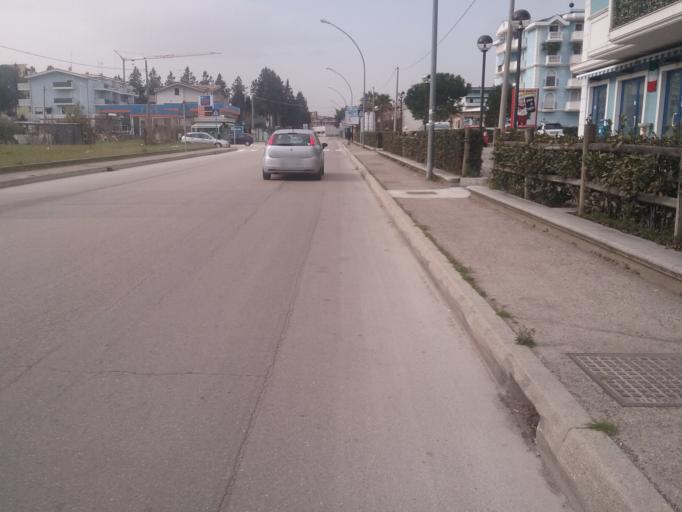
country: IT
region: Abruzzo
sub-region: Provincia di Pescara
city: Montesilvano Marina
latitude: 42.5057
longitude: 14.1436
